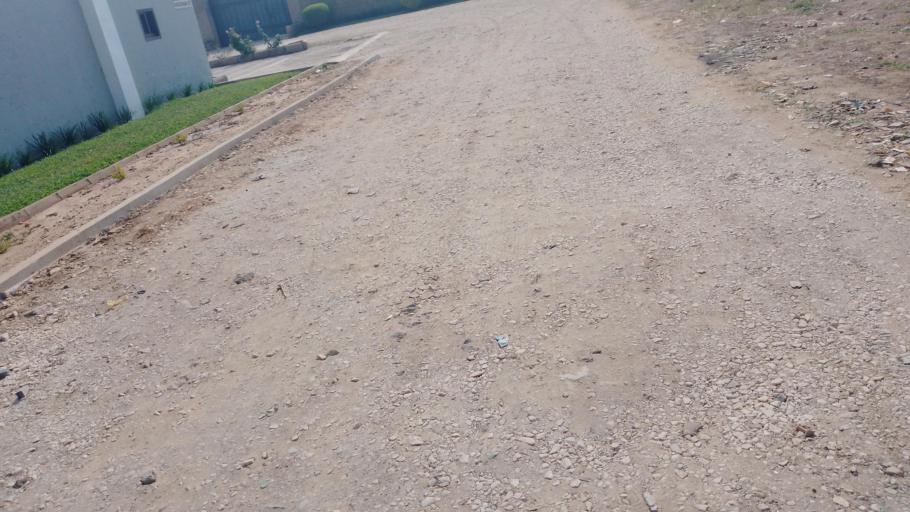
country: ZM
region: Lusaka
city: Lusaka
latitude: -15.3890
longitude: 28.3901
